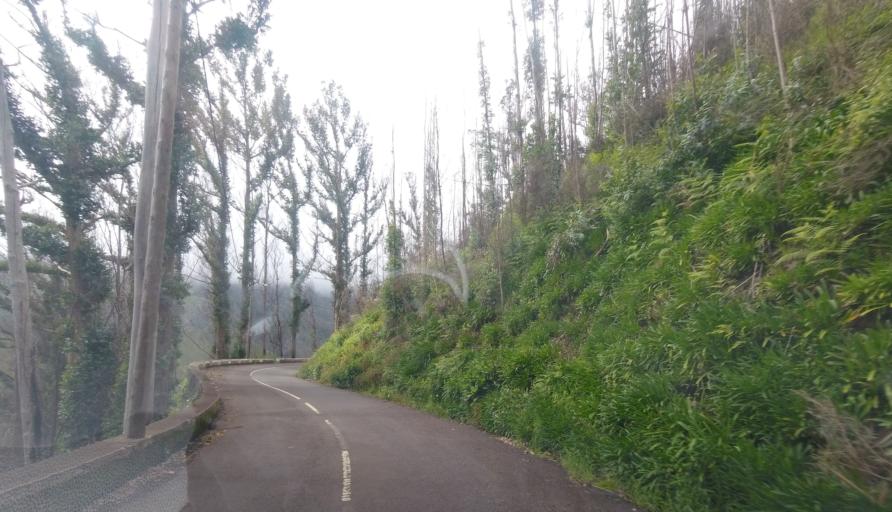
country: PT
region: Madeira
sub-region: Funchal
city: Nossa Senhora do Monte
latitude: 32.6809
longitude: -16.8907
